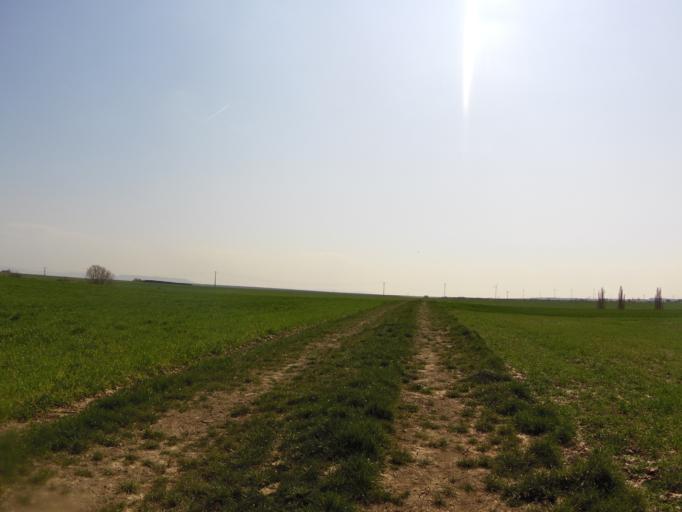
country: DE
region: Bavaria
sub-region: Regierungsbezirk Unterfranken
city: Prosselsheim
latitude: 49.8194
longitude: 10.1078
